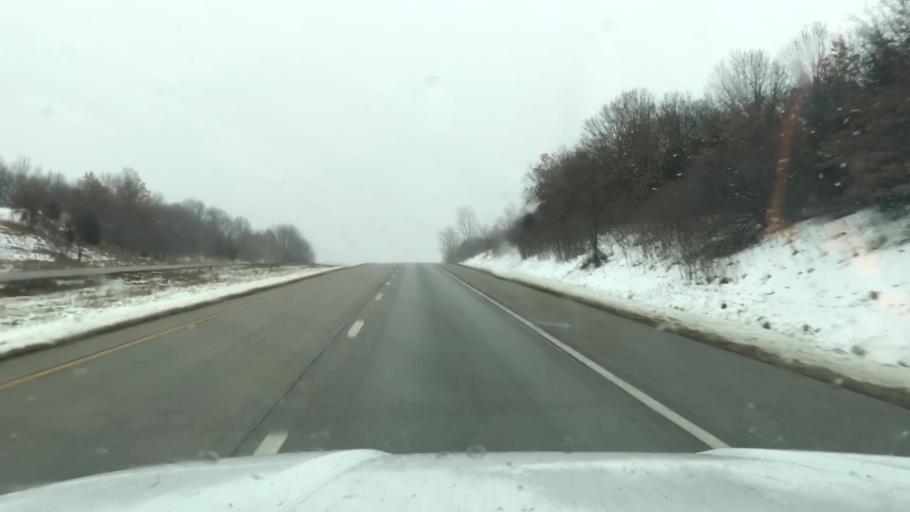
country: US
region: Missouri
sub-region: Clinton County
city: Gower
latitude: 39.7532
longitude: -94.5894
